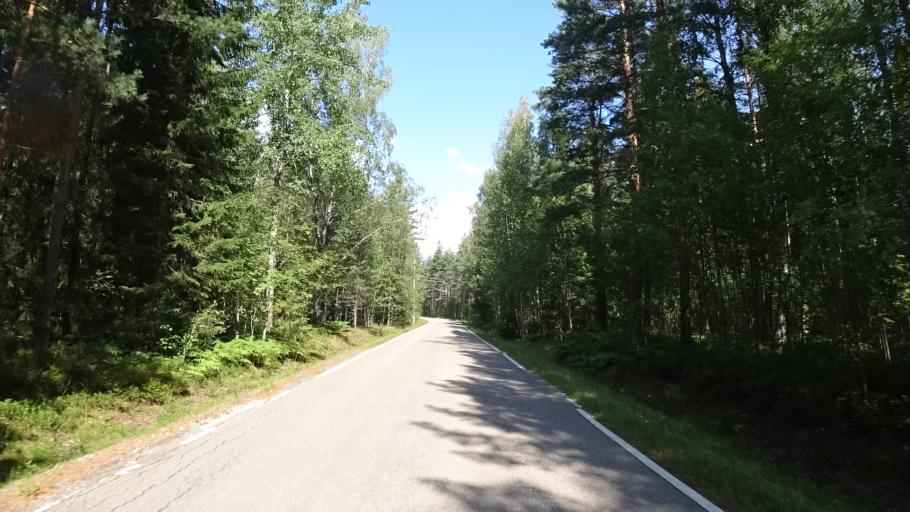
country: FI
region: Kymenlaakso
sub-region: Kotka-Hamina
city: Karhula
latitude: 60.5714
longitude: 26.8993
